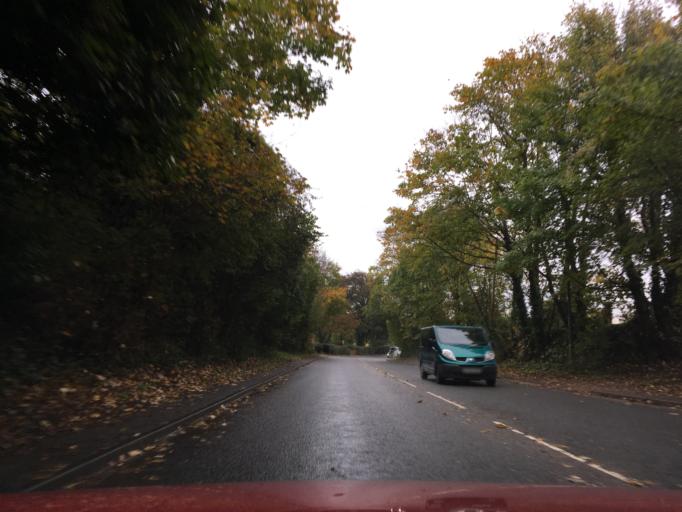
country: GB
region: Wales
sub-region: Monmouthshire
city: Magor
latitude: 51.5843
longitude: -2.8382
